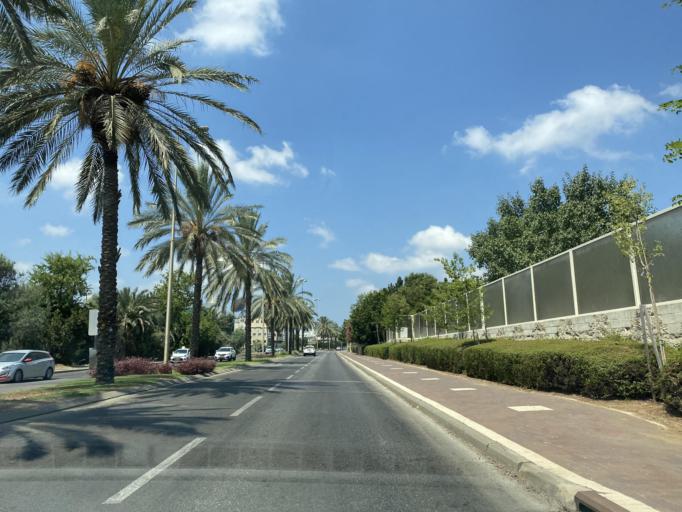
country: IL
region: Central District
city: Kfar Saba
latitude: 32.1771
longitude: 34.9331
